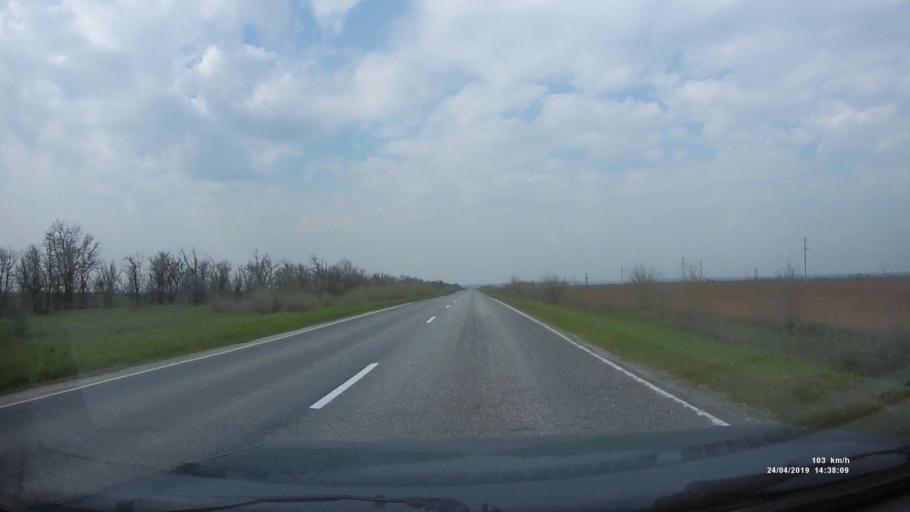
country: RU
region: Rostov
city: Remontnoye
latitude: 46.3962
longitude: 43.8861
